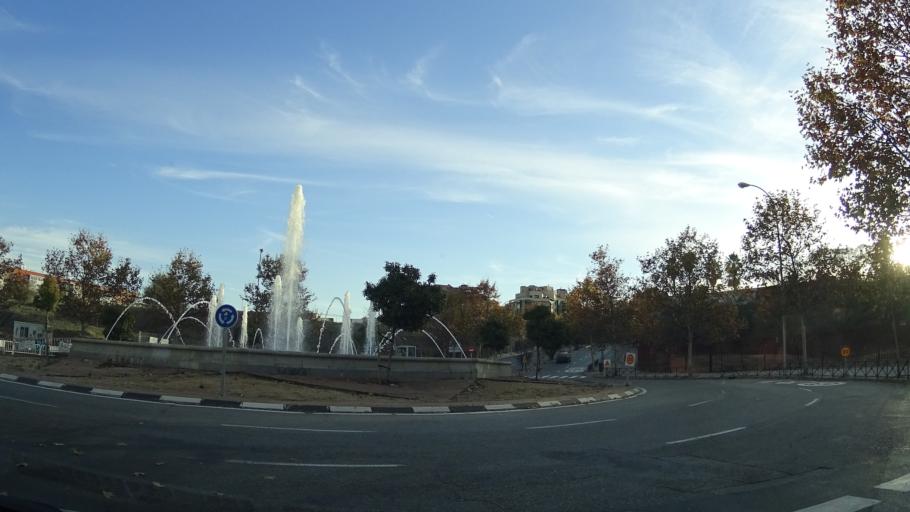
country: ES
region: Madrid
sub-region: Provincia de Madrid
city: Salamanca
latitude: 40.4410
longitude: -3.6667
